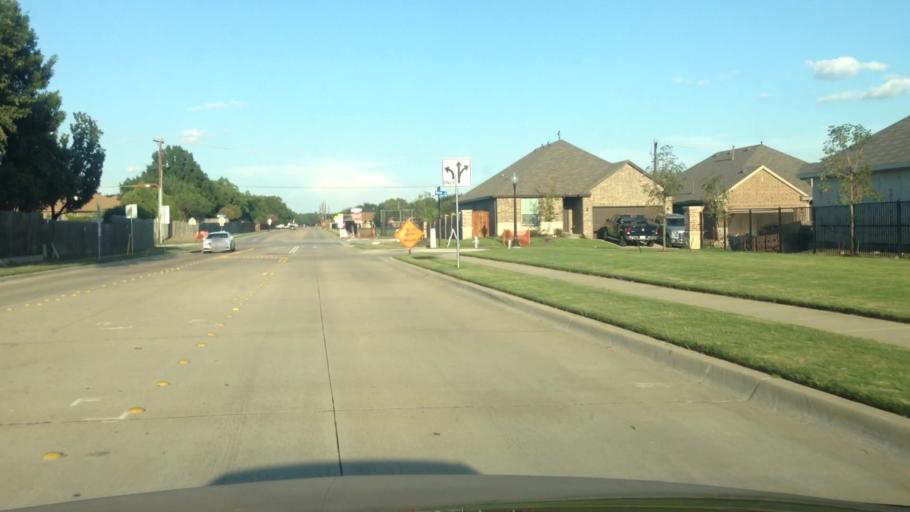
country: US
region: Texas
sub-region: Tarrant County
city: Watauga
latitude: 32.8822
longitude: -97.2560
